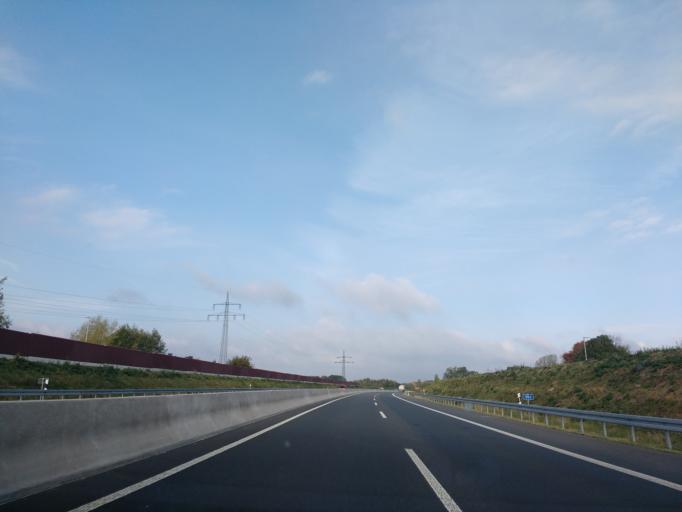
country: DE
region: North Rhine-Westphalia
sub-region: Regierungsbezirk Detmold
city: Steinhagen
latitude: 51.9880
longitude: 8.4509
